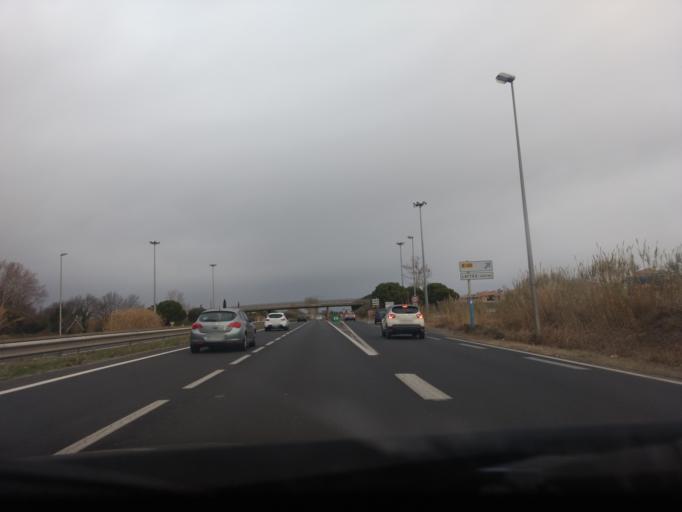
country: FR
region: Languedoc-Roussillon
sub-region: Departement de l'Herault
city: Lattes
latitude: 43.5697
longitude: 3.8958
